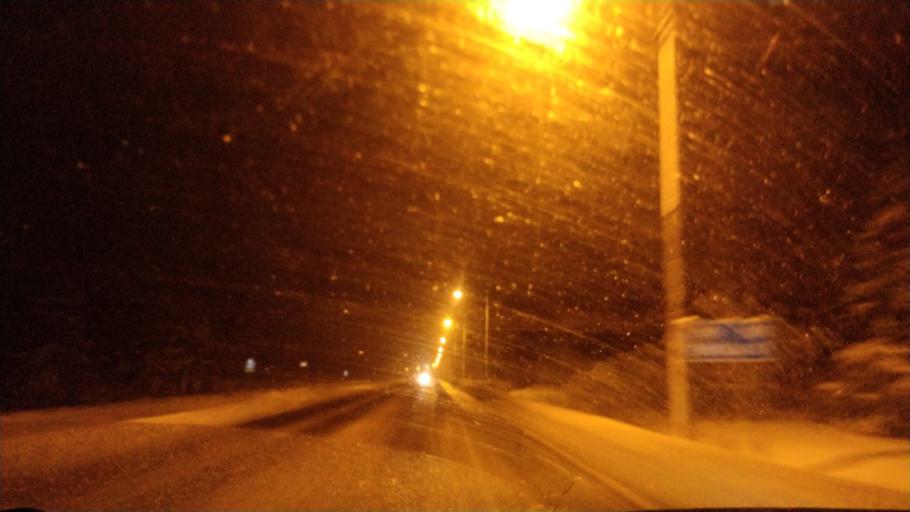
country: FI
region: Lapland
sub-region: Rovaniemi
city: Rovaniemi
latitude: 66.4081
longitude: 25.3990
